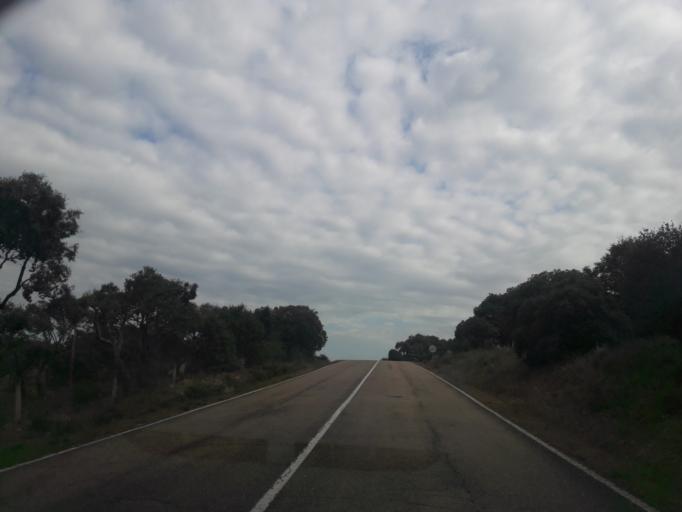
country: ES
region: Castille and Leon
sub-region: Provincia de Salamanca
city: Ciudad Rodrigo
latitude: 40.5602
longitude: -6.5285
